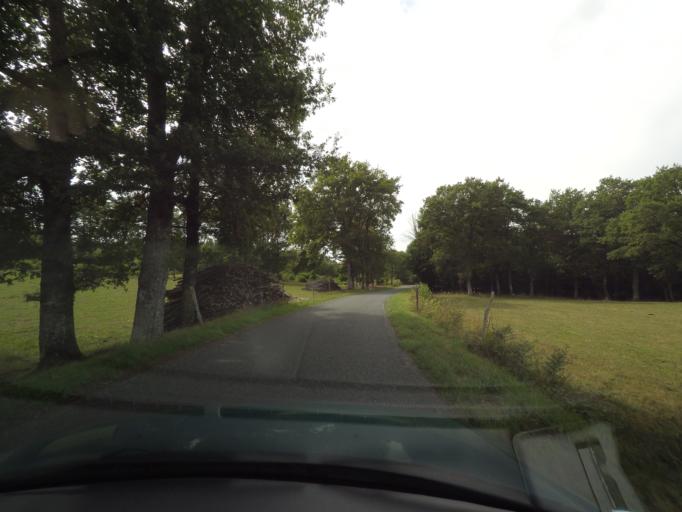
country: FR
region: Limousin
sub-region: Departement de la Haute-Vienne
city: Ladignac-le-Long
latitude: 45.6471
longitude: 1.1040
